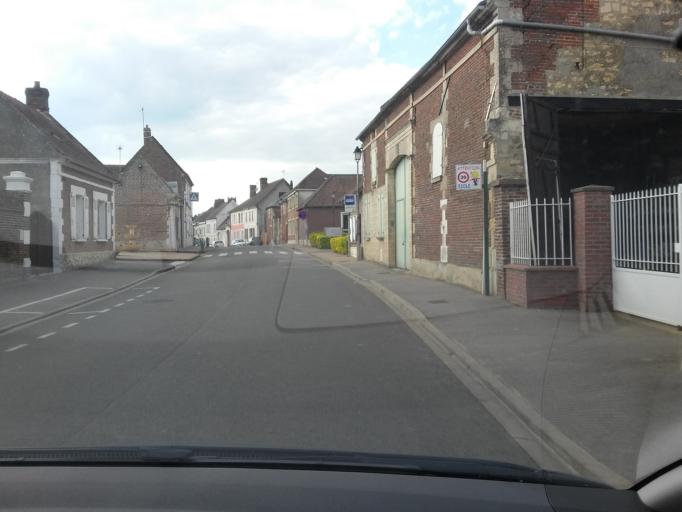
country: FR
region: Picardie
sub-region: Departement de l'Oise
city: Grandfresnoy
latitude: 49.3711
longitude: 2.6536
